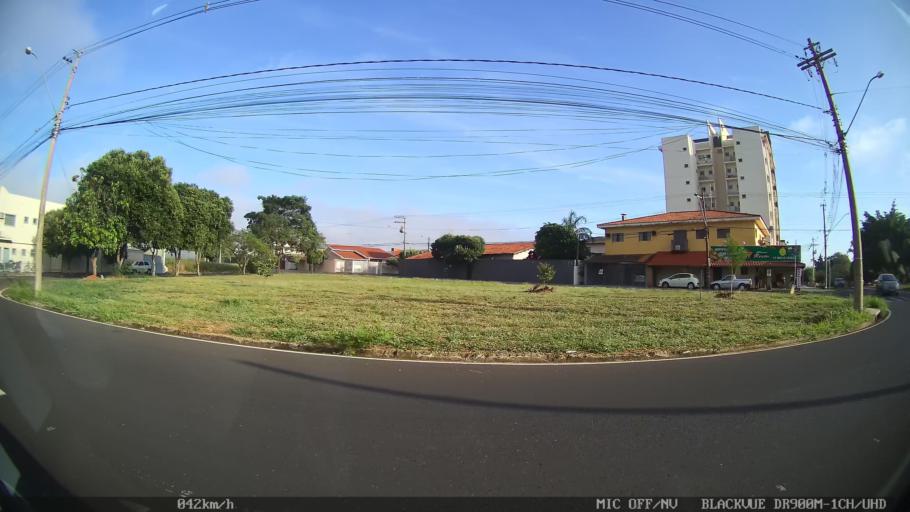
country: BR
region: Sao Paulo
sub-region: Sao Jose Do Rio Preto
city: Sao Jose do Rio Preto
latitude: -20.8338
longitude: -49.3657
